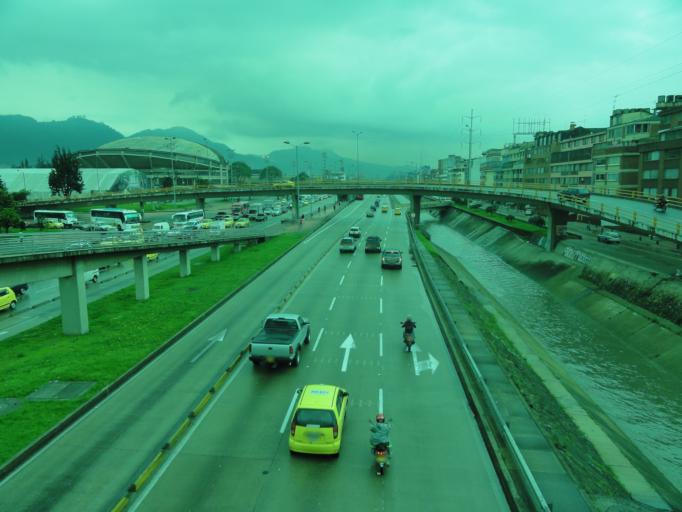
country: CO
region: Bogota D.C.
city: Bogota
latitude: 4.6520
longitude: -74.0783
